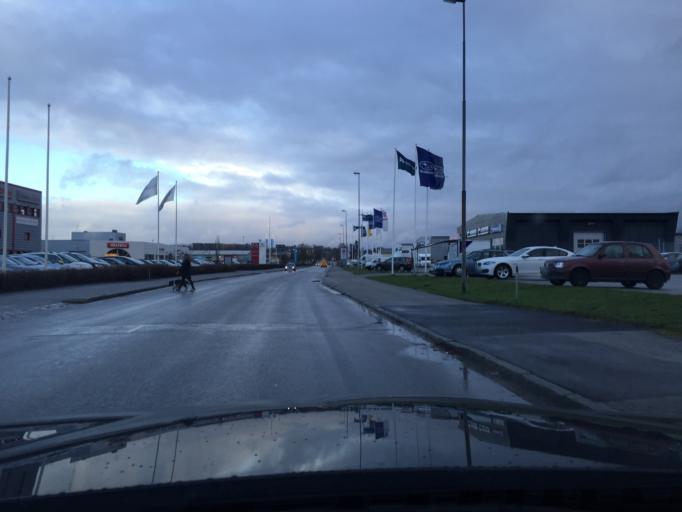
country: SE
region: Skane
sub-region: Lunds Kommun
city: Lund
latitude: 55.6909
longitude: 13.2187
